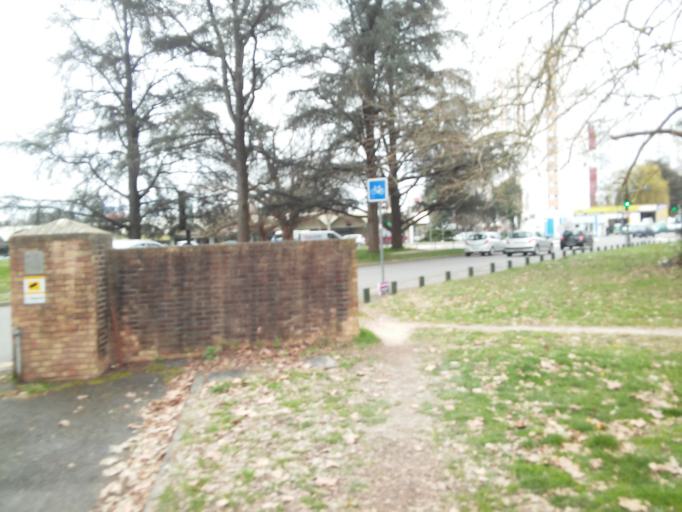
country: FR
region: Aquitaine
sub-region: Departement des Pyrenees-Atlantiques
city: Pau
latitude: 43.3121
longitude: -0.3652
